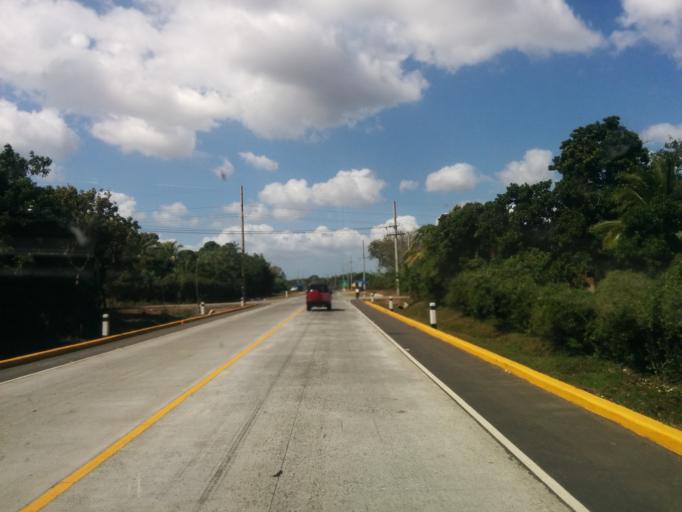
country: NI
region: Masaya
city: Masaya
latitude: 11.9942
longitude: -86.0785
